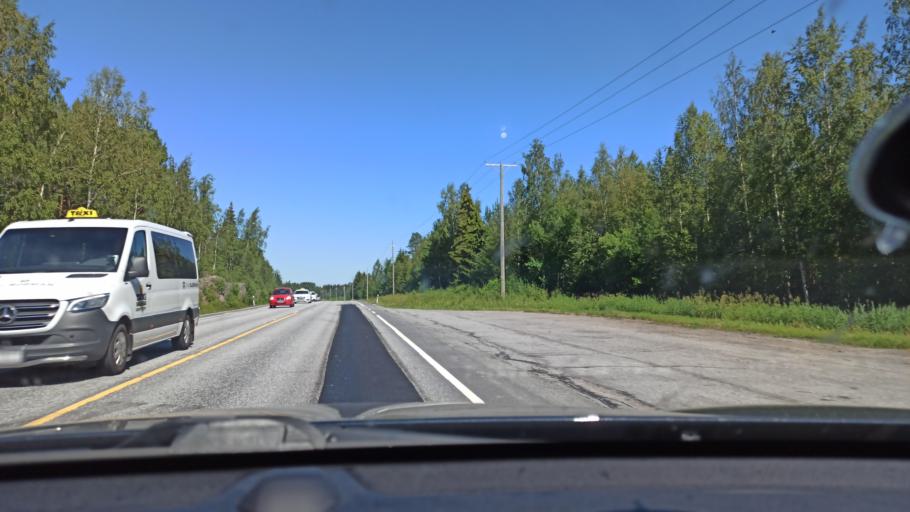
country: FI
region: Ostrobothnia
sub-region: Vaasa
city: Voera
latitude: 63.2164
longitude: 22.2096
